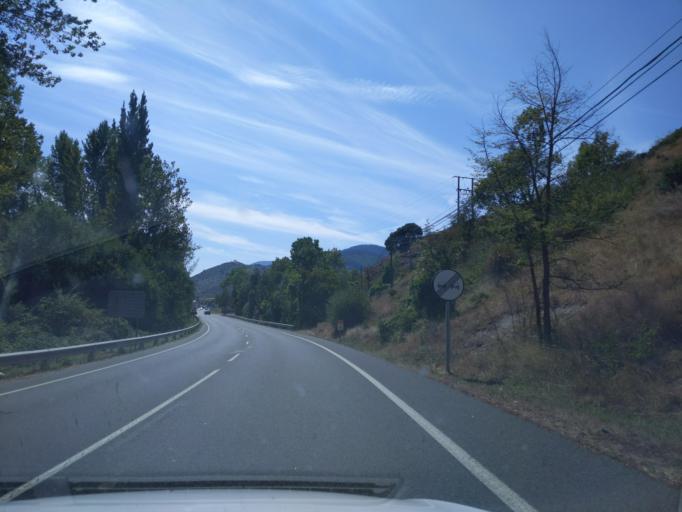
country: ES
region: La Rioja
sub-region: Provincia de La Rioja
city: Ojacastro
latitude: 42.3392
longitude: -3.0093
